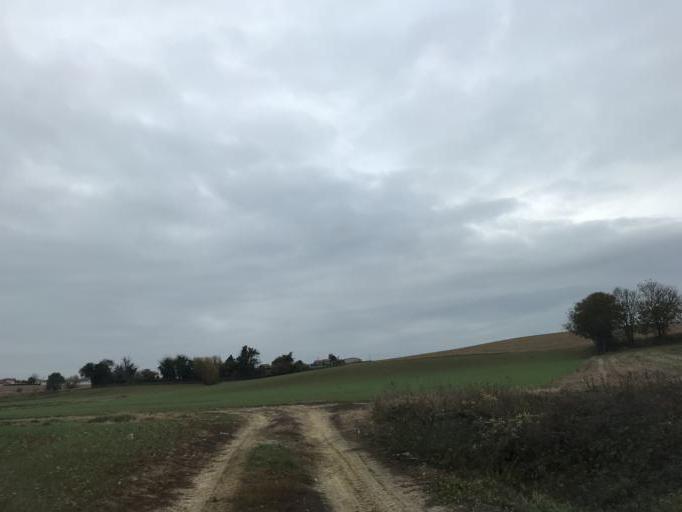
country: FR
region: Rhone-Alpes
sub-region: Departement de l'Ain
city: Miribel
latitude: 45.8371
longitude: 4.9392
